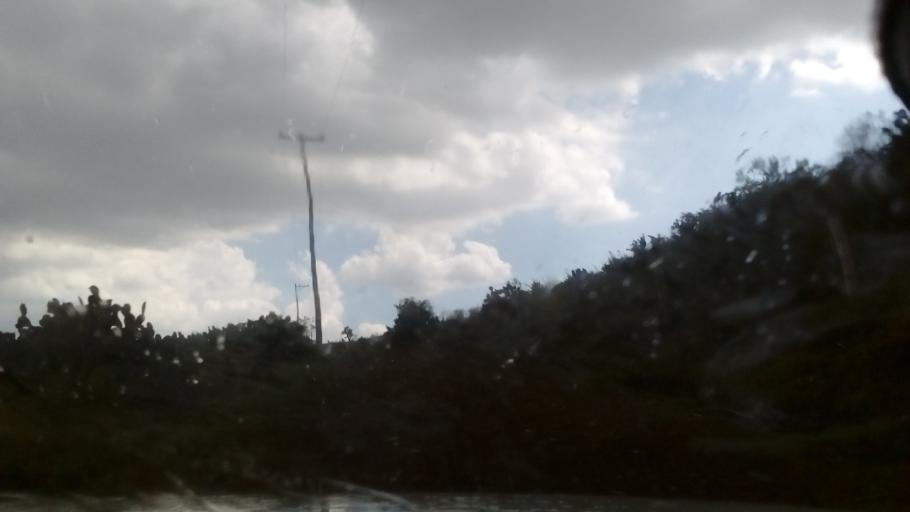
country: MX
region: Guanajuato
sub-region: Silao de la Victoria
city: San Francisco (Banos de Agua Caliente)
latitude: 21.1494
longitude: -101.4364
